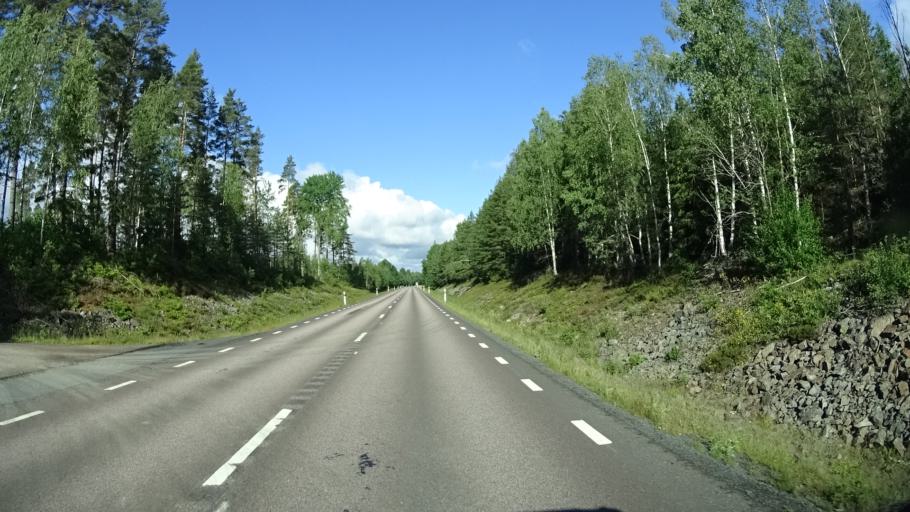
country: SE
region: Kalmar
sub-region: Hogsby Kommun
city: Hoegsby
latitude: 57.1357
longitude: 15.8412
